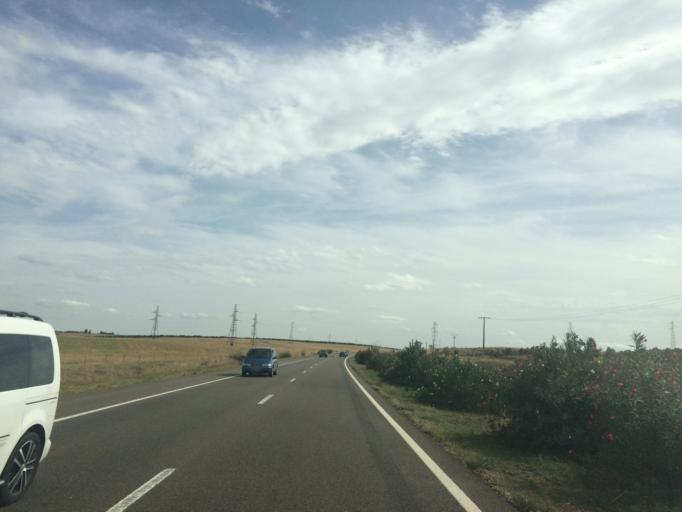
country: MA
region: Meknes-Tafilalet
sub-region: Meknes
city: Meknes
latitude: 33.8308
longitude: -5.5472
